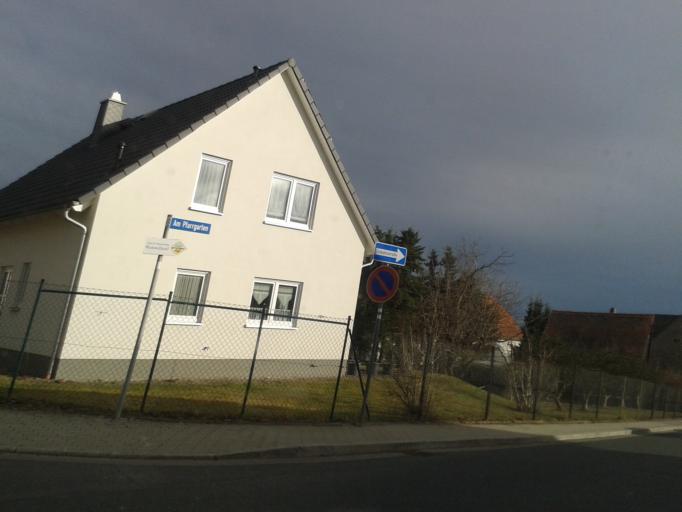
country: DE
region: Saxony
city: Freital
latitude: 51.0286
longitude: 13.6517
